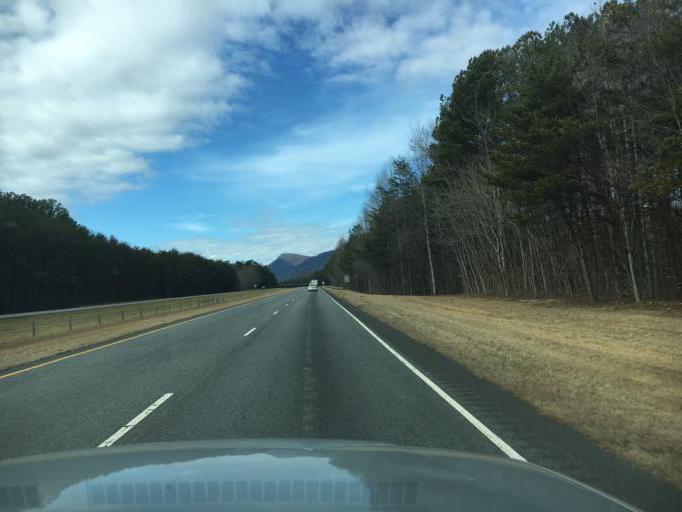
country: US
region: North Carolina
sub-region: Polk County
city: Columbus
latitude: 35.2702
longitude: -82.1525
